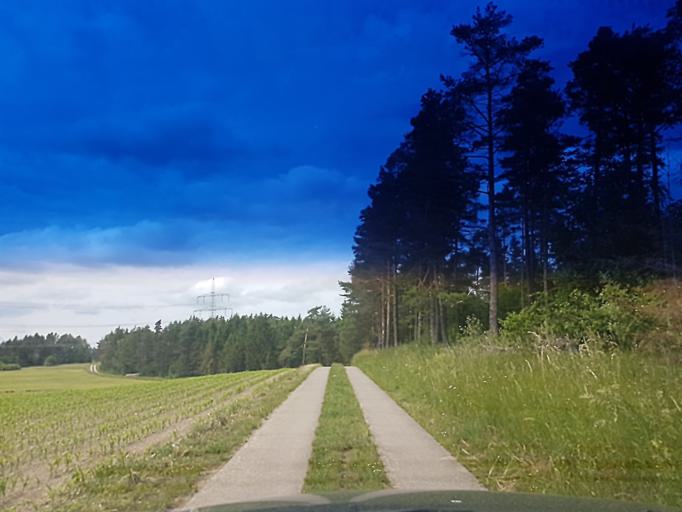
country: DE
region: Bavaria
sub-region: Upper Franconia
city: Wattendorf
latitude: 50.0082
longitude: 11.1240
